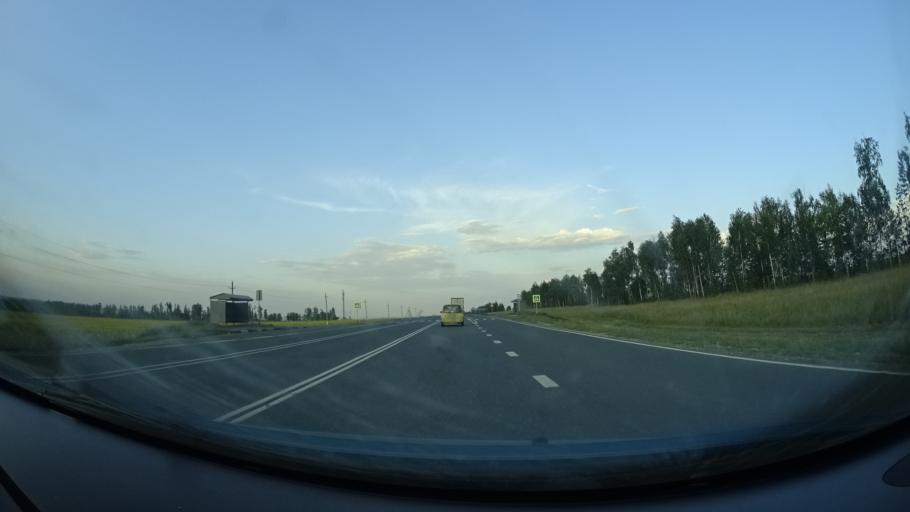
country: RU
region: Samara
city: Kamyshla
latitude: 54.0774
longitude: 52.3267
